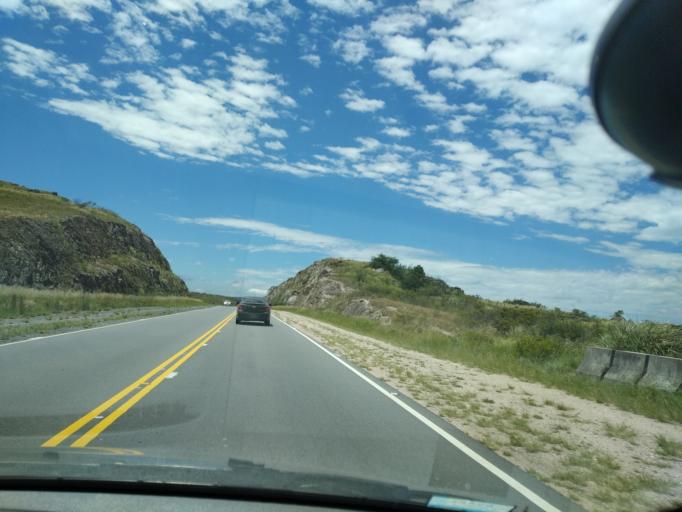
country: AR
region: Cordoba
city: Cuesta Blanca
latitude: -31.5786
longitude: -64.6396
